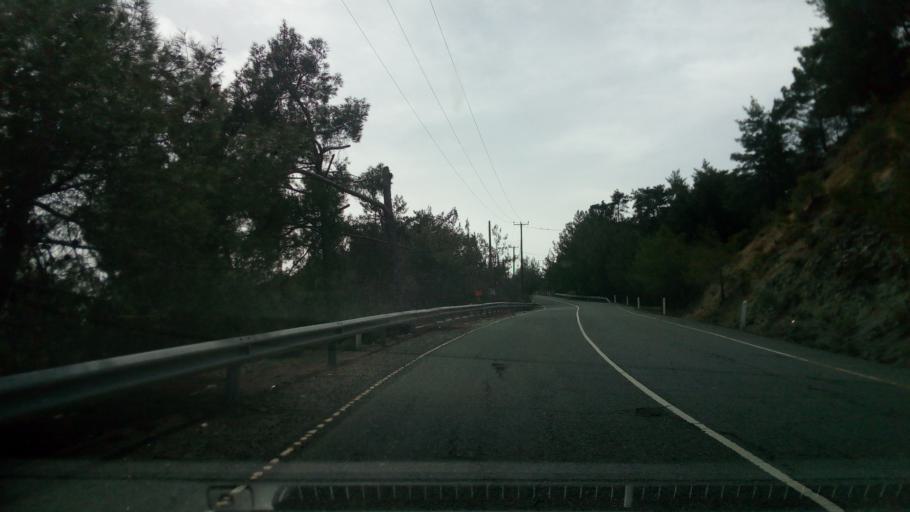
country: CY
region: Limassol
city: Pelendri
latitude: 34.8883
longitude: 32.9550
